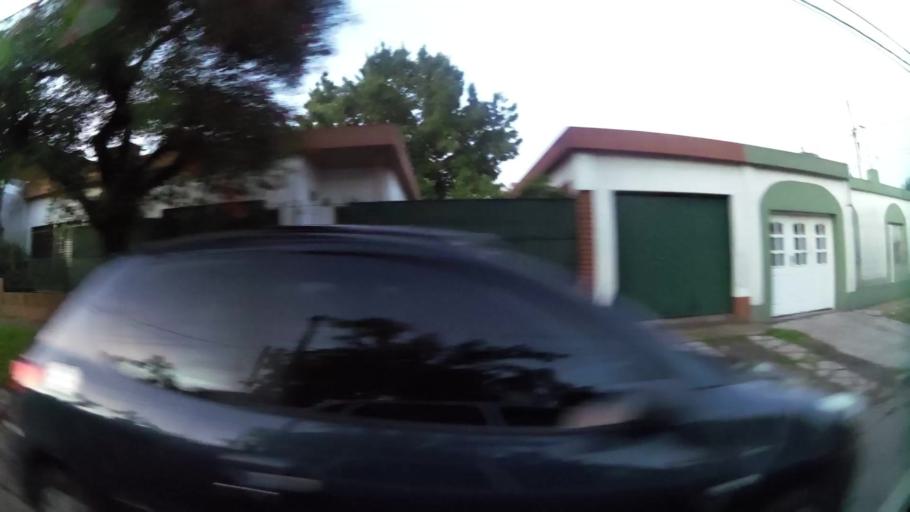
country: AR
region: Buenos Aires
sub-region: Partido de Moron
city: Moron
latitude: -34.6544
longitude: -58.6324
